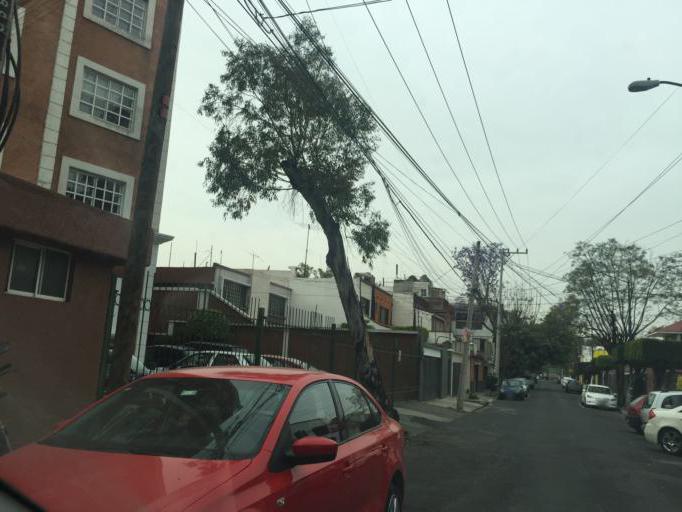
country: MX
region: Mexico
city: Colonia Lindavista
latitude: 19.4938
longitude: -99.1220
